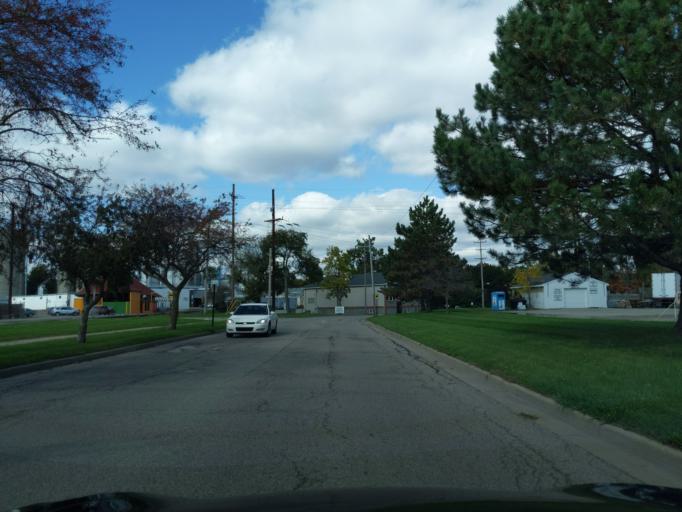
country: US
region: Michigan
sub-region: Eaton County
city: Charlotte
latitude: 42.5680
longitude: -84.8340
